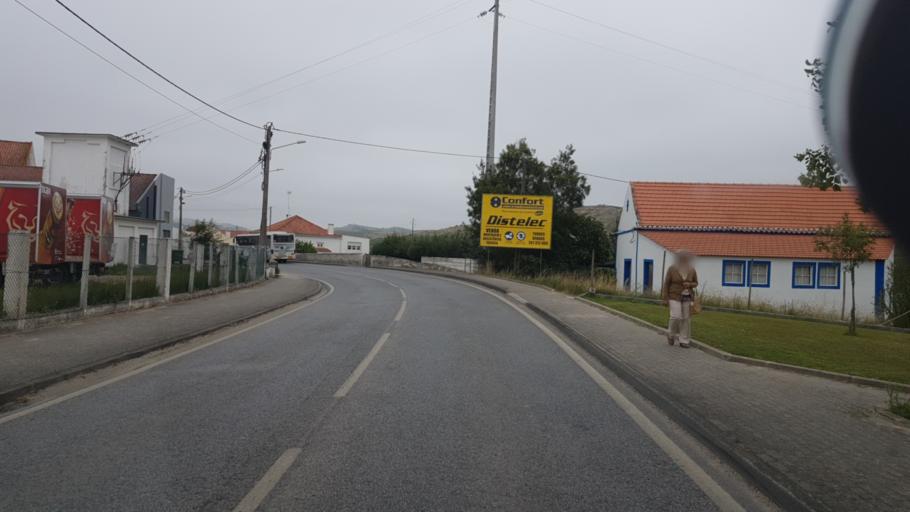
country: PT
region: Lisbon
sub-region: Torres Vedras
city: Silveira
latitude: 39.0895
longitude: -9.3173
